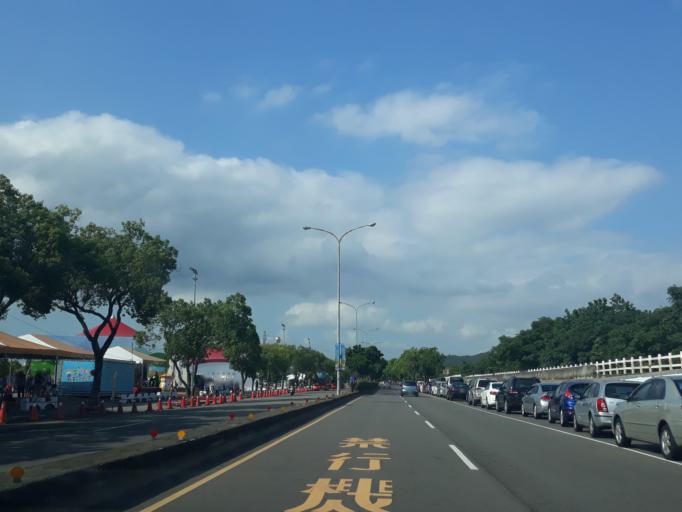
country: TW
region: Taiwan
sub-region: Miaoli
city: Miaoli
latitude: 24.5781
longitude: 120.8429
